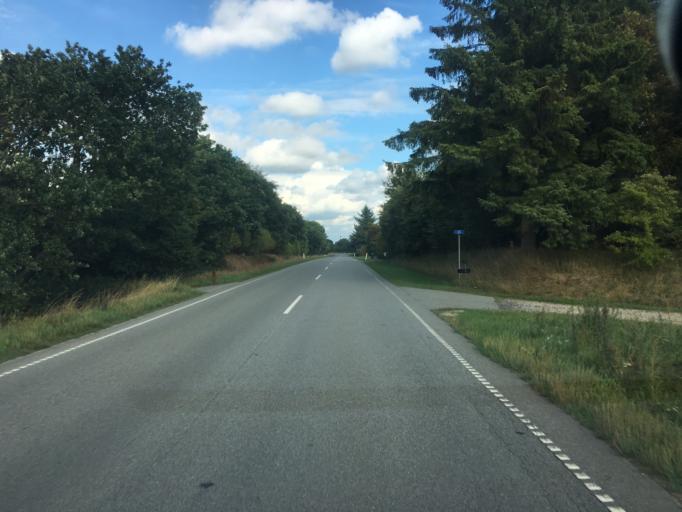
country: DK
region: South Denmark
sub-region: Tonder Kommune
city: Logumkloster
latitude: 55.0486
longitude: 8.9351
